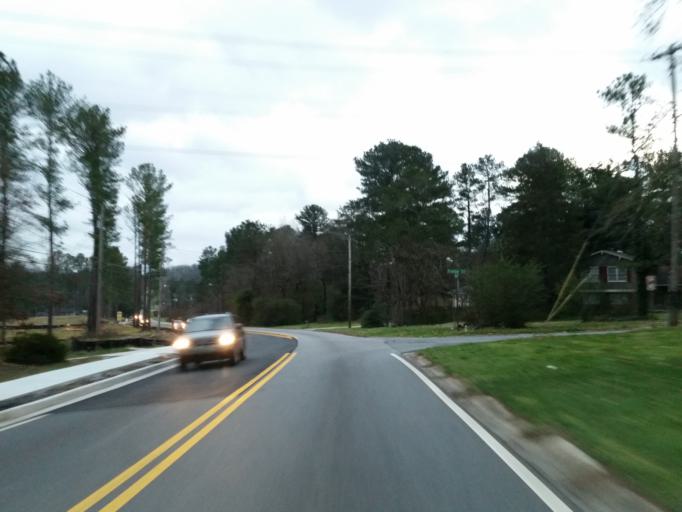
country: US
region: Georgia
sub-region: Cobb County
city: Fair Oaks
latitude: 33.8748
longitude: -84.5798
